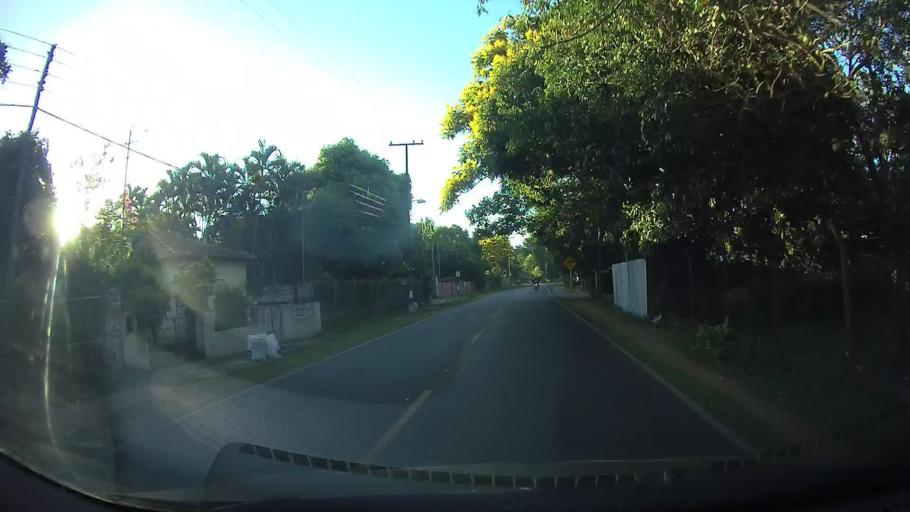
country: PY
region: Central
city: Aregua
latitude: -25.2792
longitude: -57.4028
